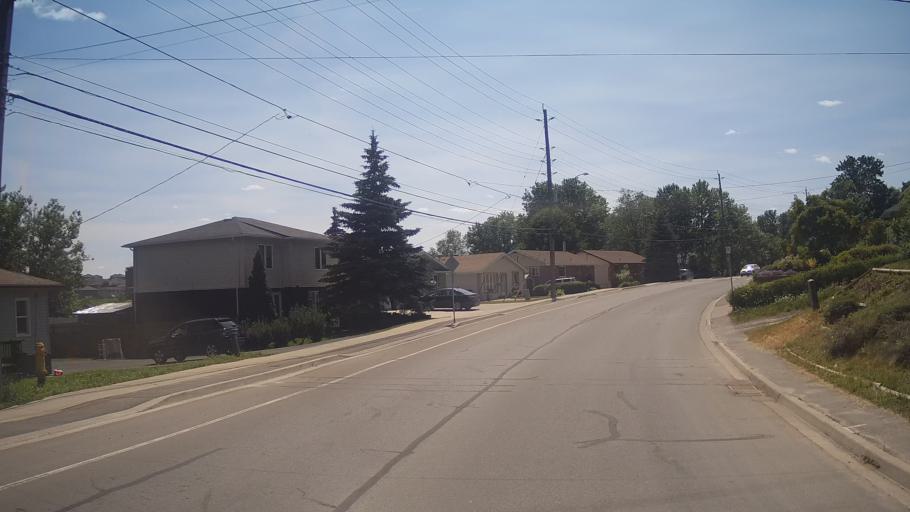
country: CA
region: Ontario
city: Greater Sudbury
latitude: 46.4605
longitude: -81.0154
